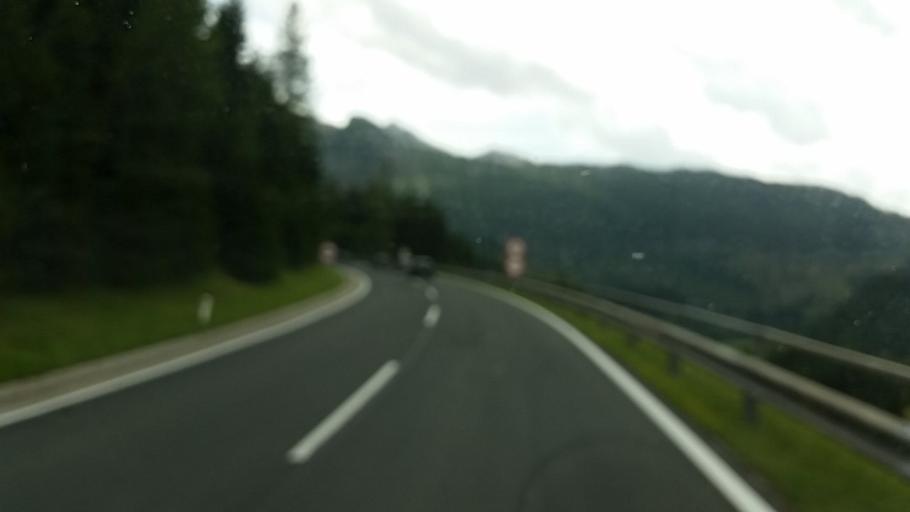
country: AT
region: Salzburg
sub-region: Politischer Bezirk Sankt Johann im Pongau
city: Untertauern
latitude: 47.2668
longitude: 13.5004
